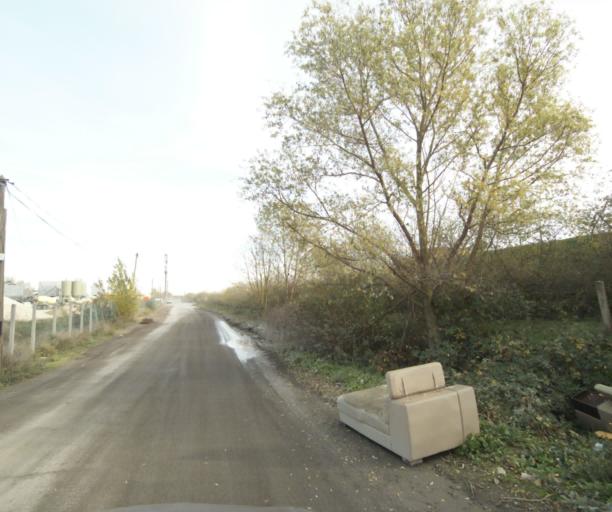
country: FR
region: Ile-de-France
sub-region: Departement des Yvelines
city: Medan
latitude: 48.9481
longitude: 2.0069
